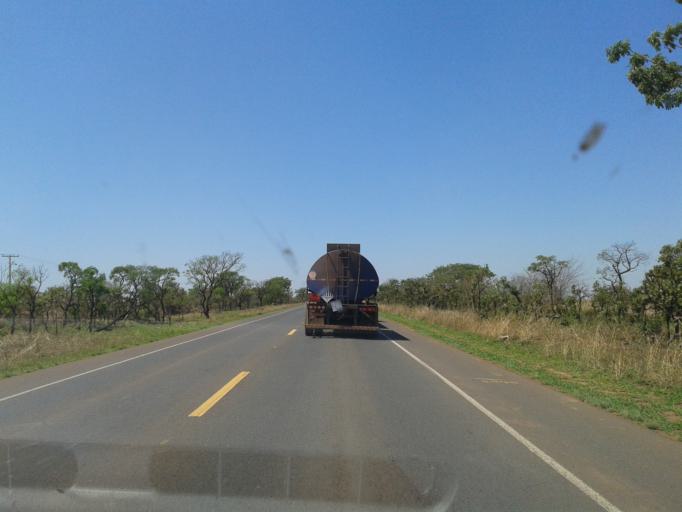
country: BR
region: Minas Gerais
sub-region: Araxa
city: Araxa
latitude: -19.3033
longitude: -47.3953
